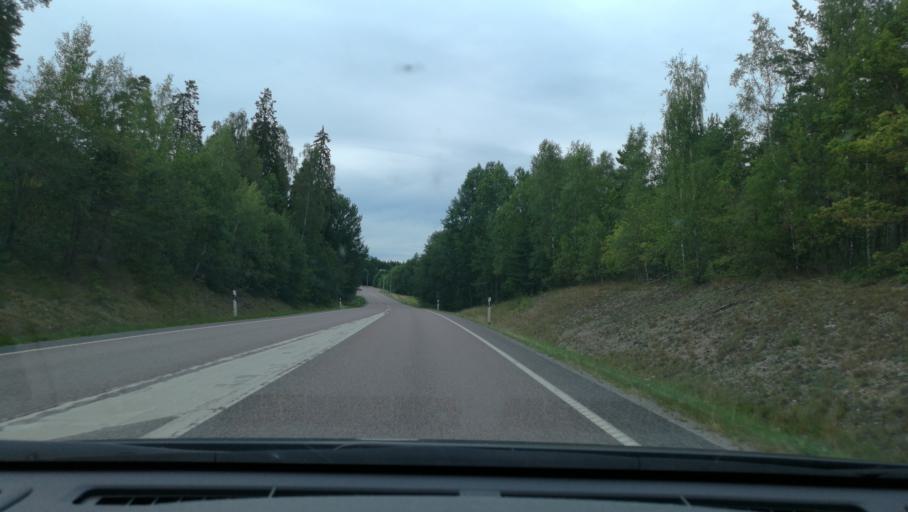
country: SE
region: Vaestmanland
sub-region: Kungsors Kommun
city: Kungsoer
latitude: 59.2802
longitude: 16.1194
